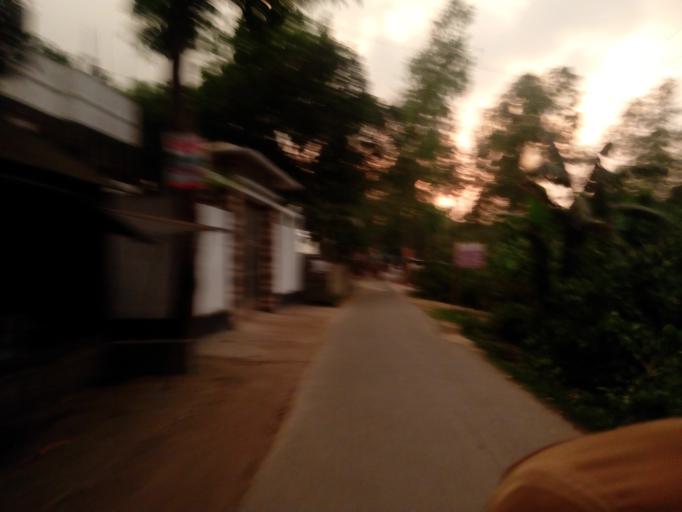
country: BD
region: Rajshahi
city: Sirajganj
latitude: 24.3027
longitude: 89.6933
